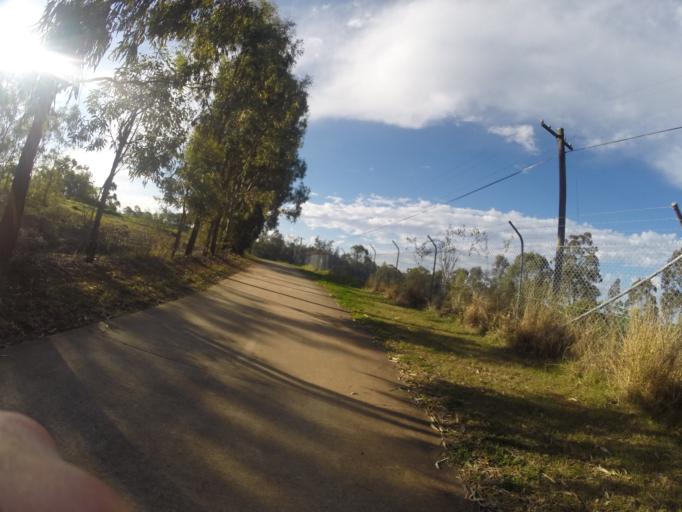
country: AU
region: New South Wales
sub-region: Fairfield
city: Horsley Park
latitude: -33.8514
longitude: 150.8683
